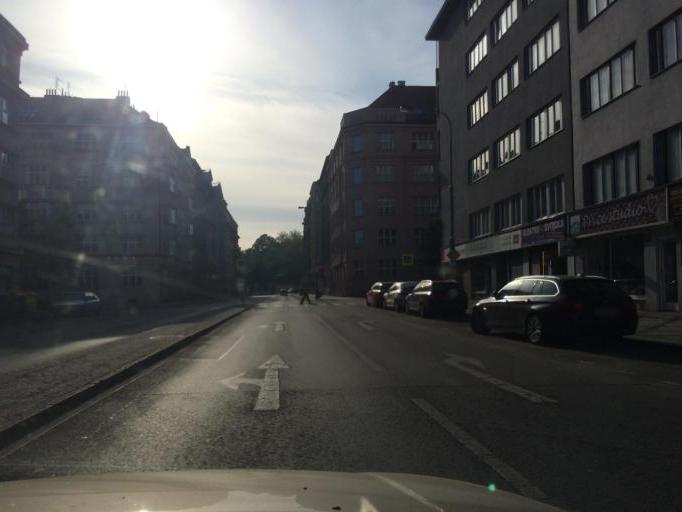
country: CZ
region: Praha
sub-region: Praha 1
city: Mala Strana
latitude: 50.1005
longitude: 14.4017
